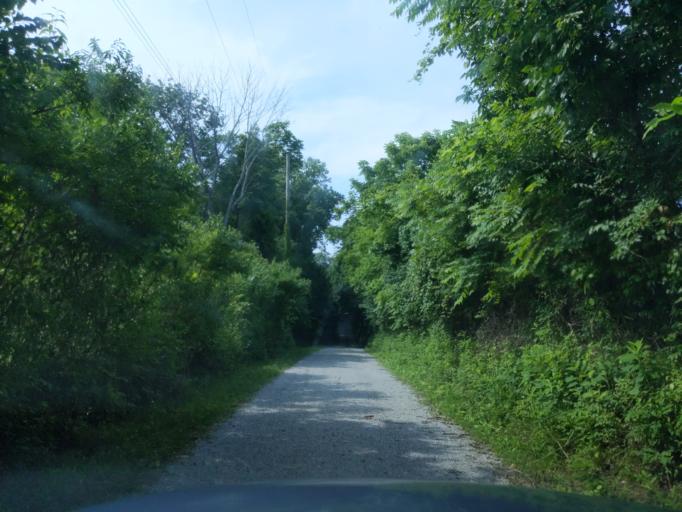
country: US
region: Tennessee
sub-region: Williamson County
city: Brentwood Estates
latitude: 36.0164
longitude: -86.7551
